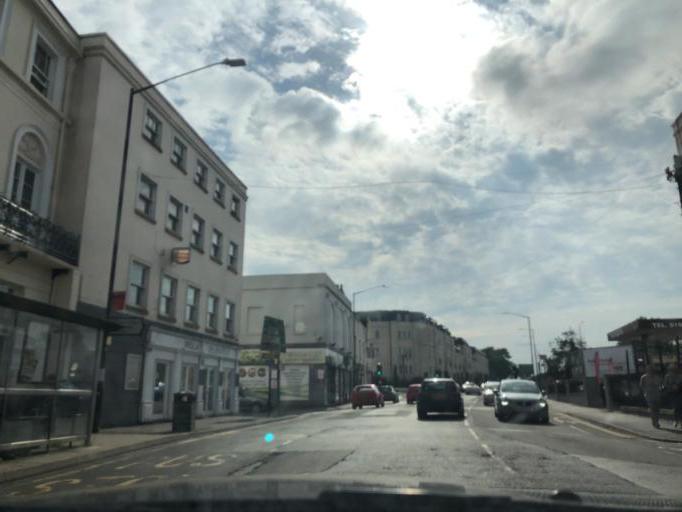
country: GB
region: England
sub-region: Warwickshire
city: Royal Leamington Spa
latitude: 52.2841
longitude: -1.5328
